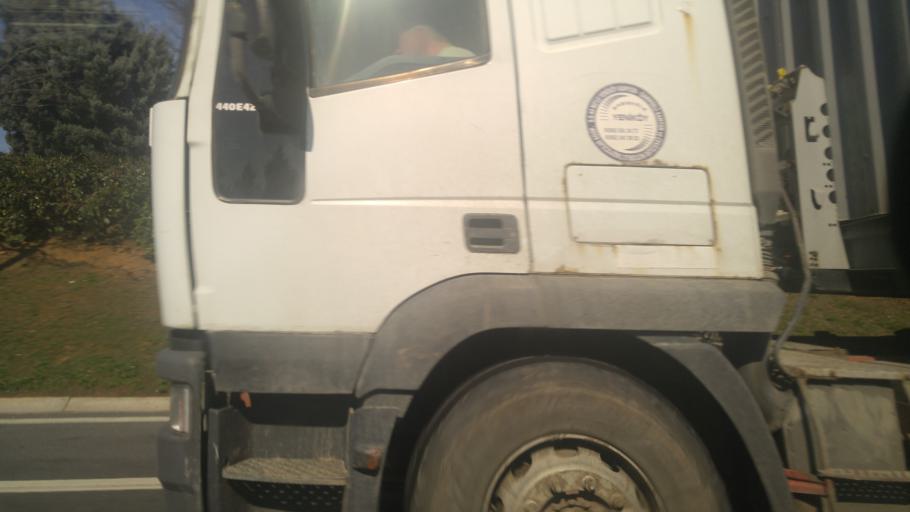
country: TR
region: Kocaeli
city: Balcik
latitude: 40.8663
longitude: 29.3878
